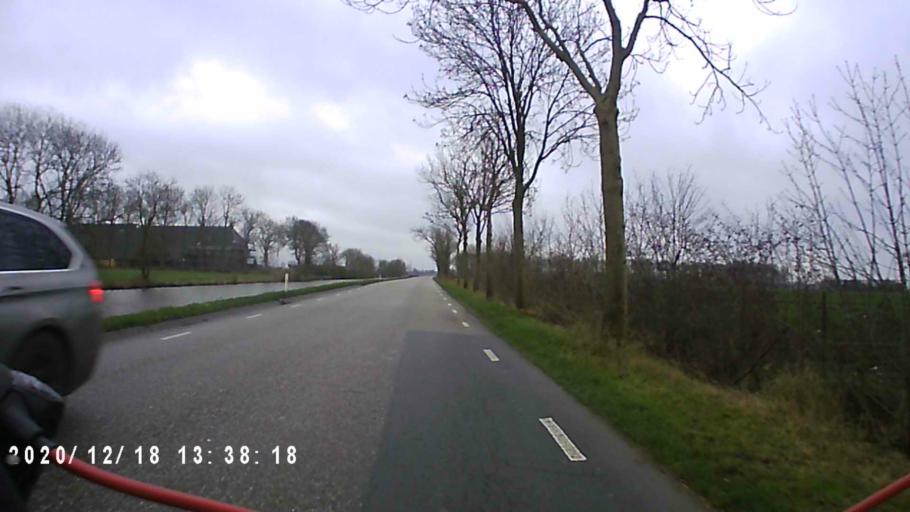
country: NL
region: Groningen
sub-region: Gemeente Bedum
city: Bedum
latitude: 53.3305
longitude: 6.5923
